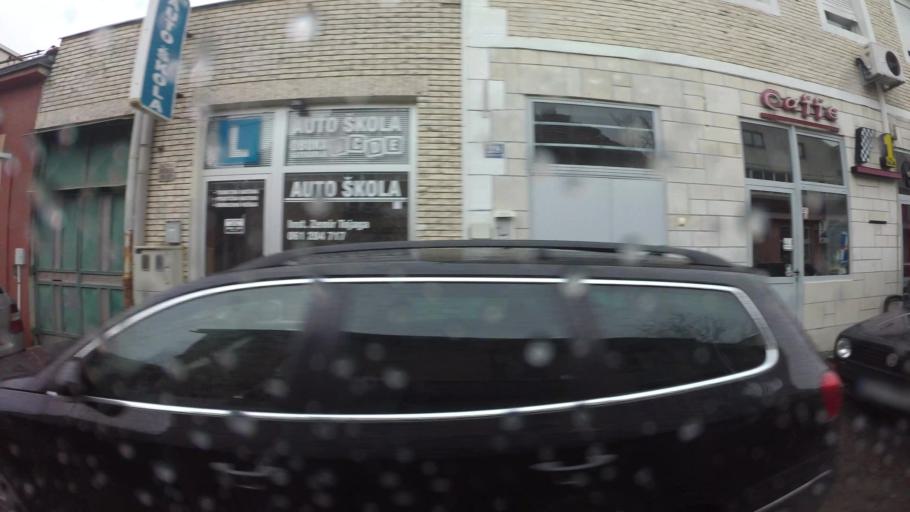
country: BA
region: Federation of Bosnia and Herzegovina
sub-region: Hercegovacko-Bosanski Kanton
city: Mostar
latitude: 43.3459
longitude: 17.8125
